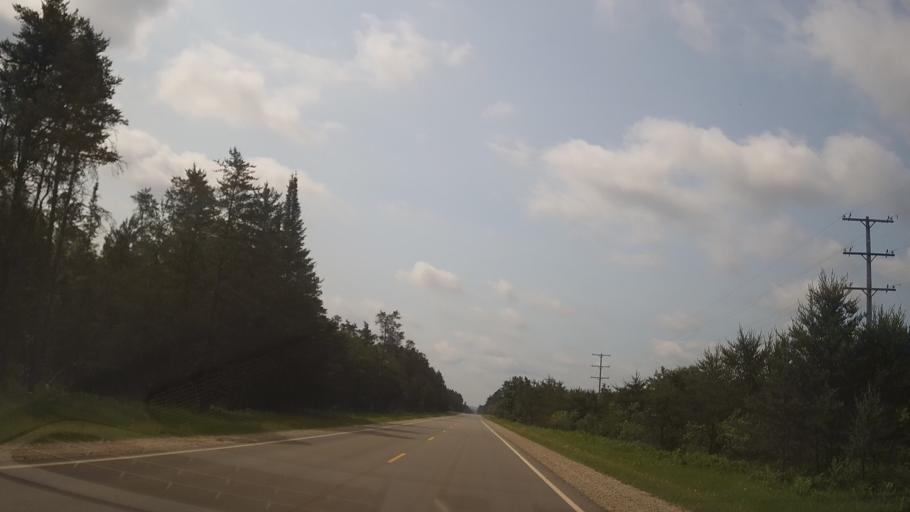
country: US
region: Michigan
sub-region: Roscommon County
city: Saint Helen
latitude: 44.4045
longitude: -84.4103
